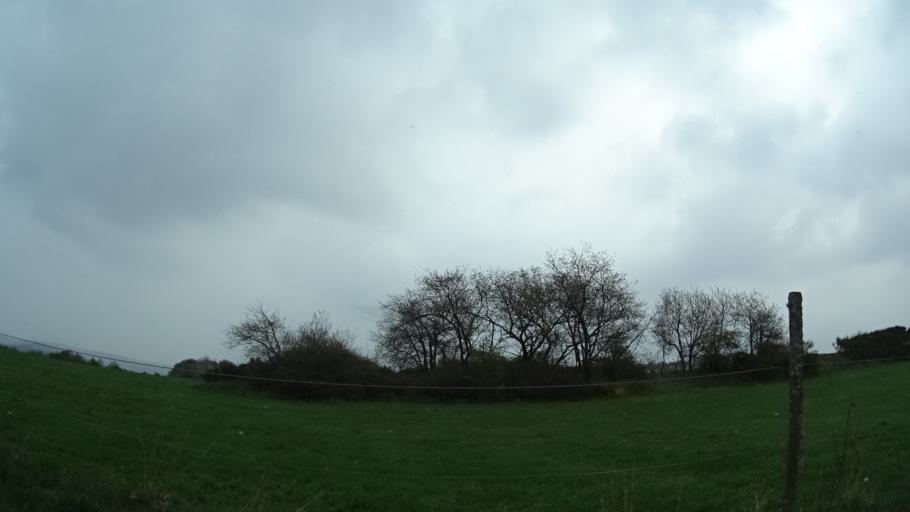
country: DE
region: Rheinland-Pfalz
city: Vollmersbach
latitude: 49.7438
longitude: 7.3186
